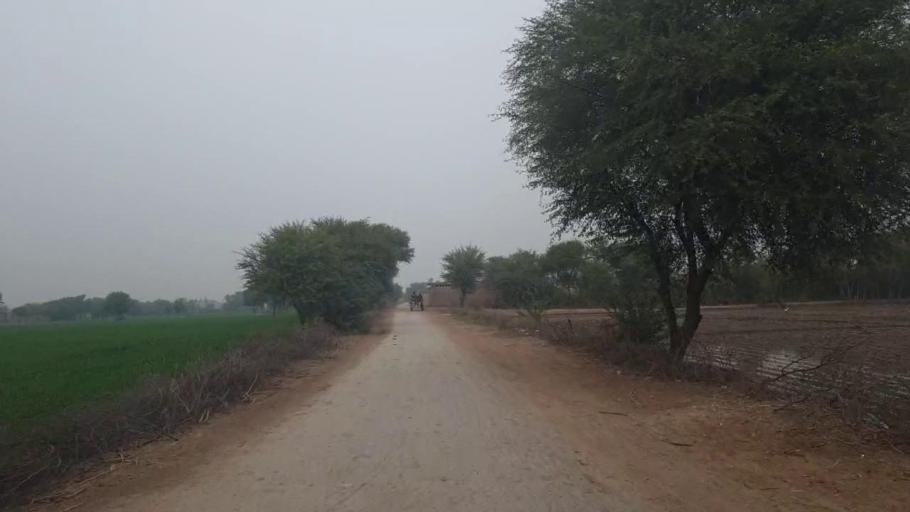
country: PK
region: Sindh
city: Tando Adam
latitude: 25.7780
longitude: 68.6985
